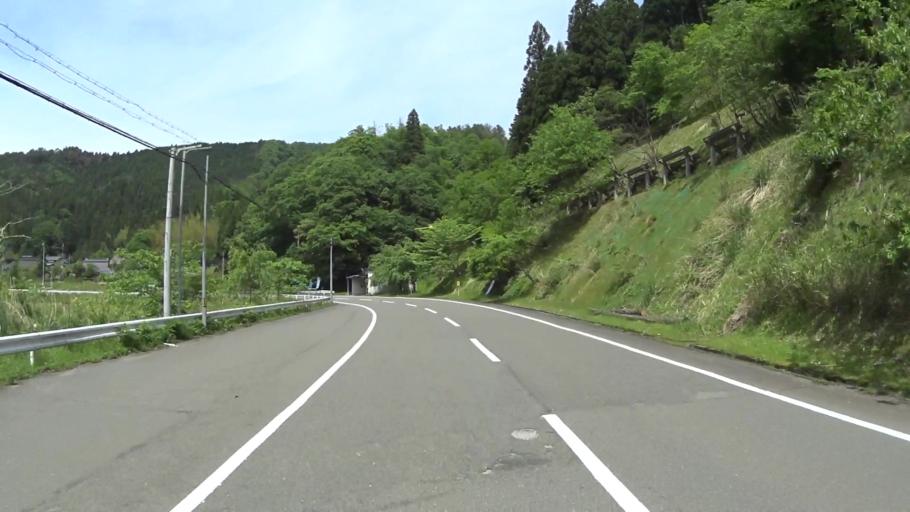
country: JP
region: Kyoto
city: Maizuru
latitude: 35.4060
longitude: 135.4645
